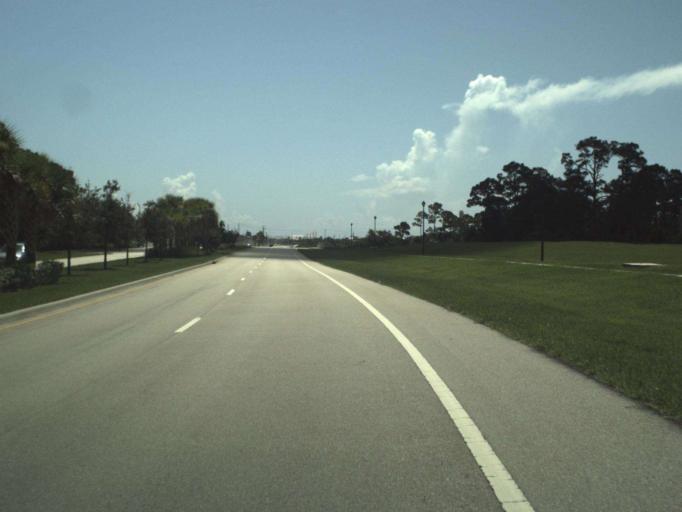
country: US
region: Florida
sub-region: Indian River County
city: Gifford
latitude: 27.6898
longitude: -80.4228
